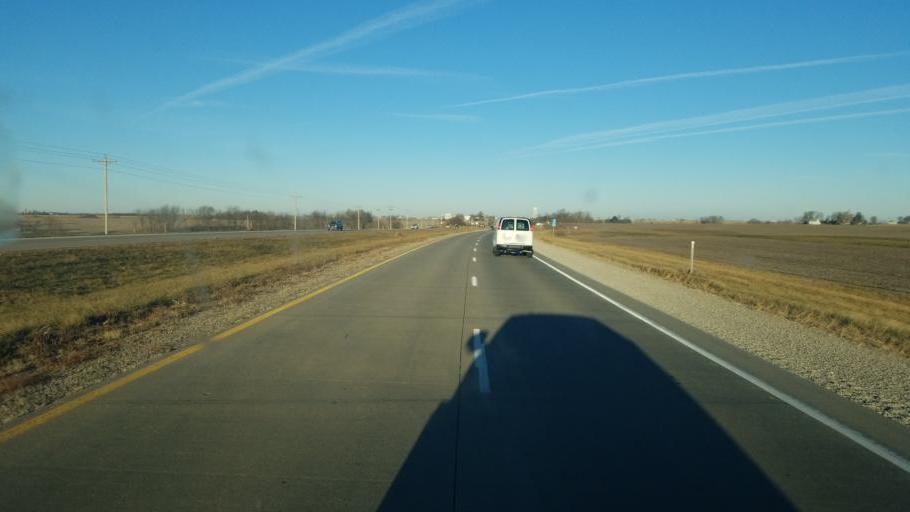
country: US
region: Iowa
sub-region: Mahaska County
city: Oskaloosa
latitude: 41.3161
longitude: -92.6917
